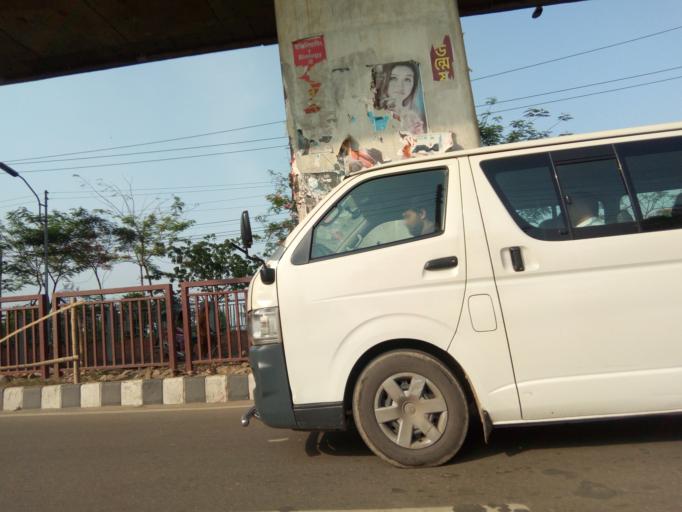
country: BD
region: Dhaka
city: Paltan
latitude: 23.7524
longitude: 90.4013
